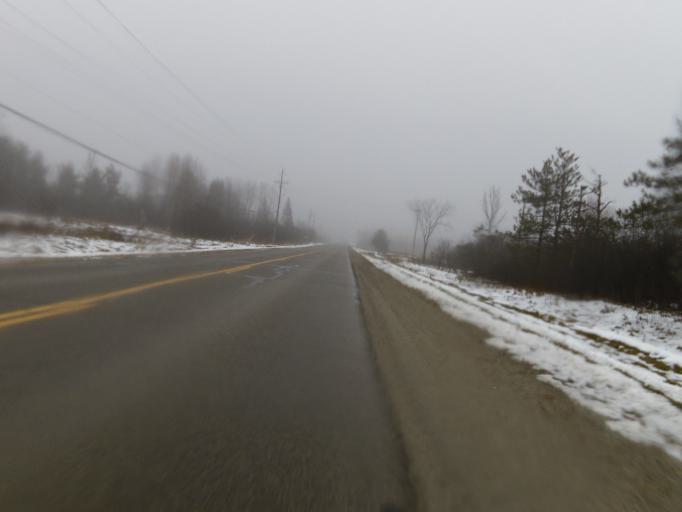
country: CA
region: Ontario
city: Perth
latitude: 44.8730
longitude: -76.3231
